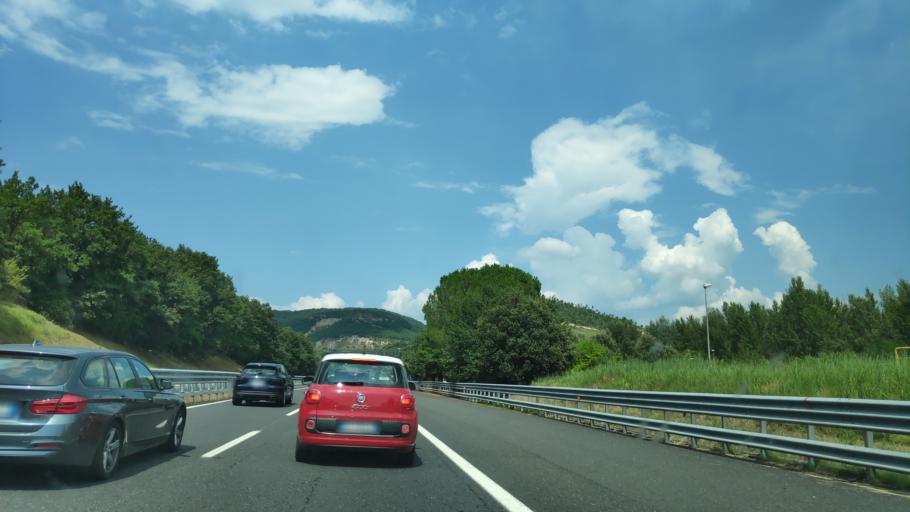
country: IT
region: Umbria
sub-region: Provincia di Terni
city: Stazione di Allerona
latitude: 42.7932
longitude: 12.0475
